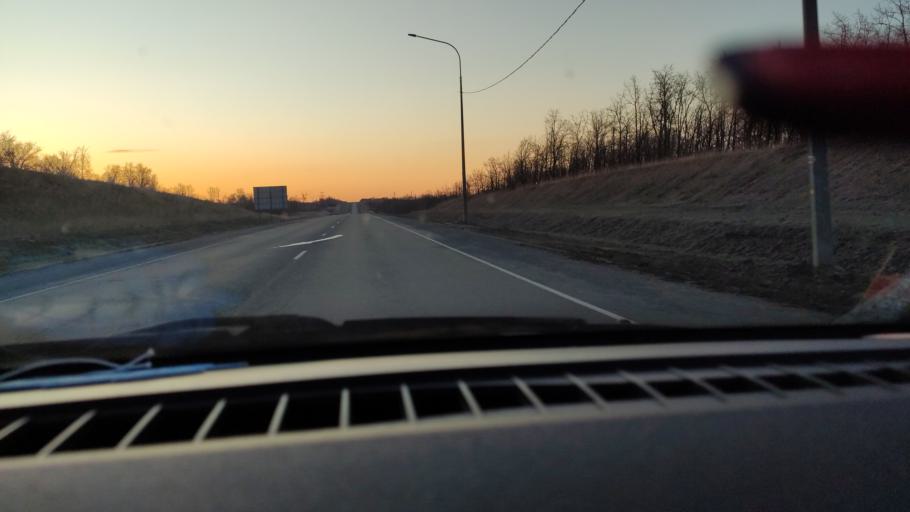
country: RU
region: Saratov
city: Yelshanka
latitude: 51.8242
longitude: 46.3060
